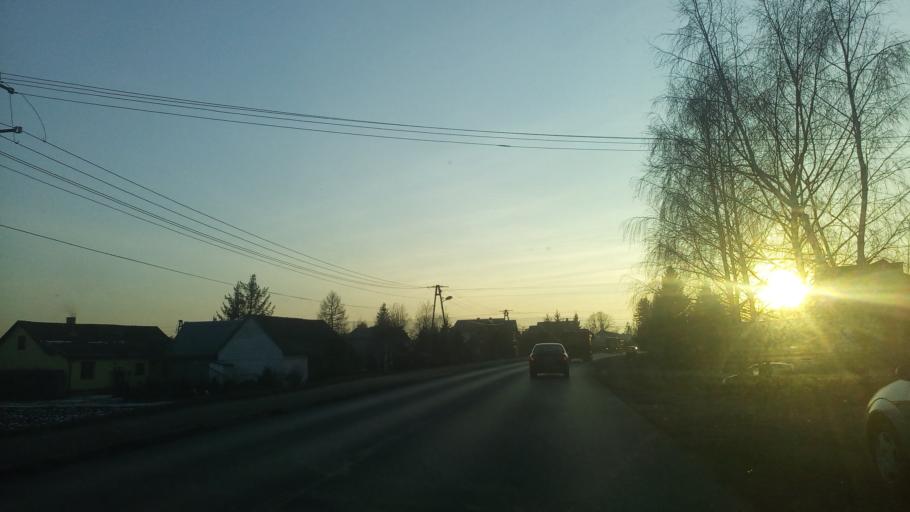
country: PL
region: Lesser Poland Voivodeship
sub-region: Powiat nowosadecki
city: Chelmiec
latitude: 49.6120
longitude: 20.6609
